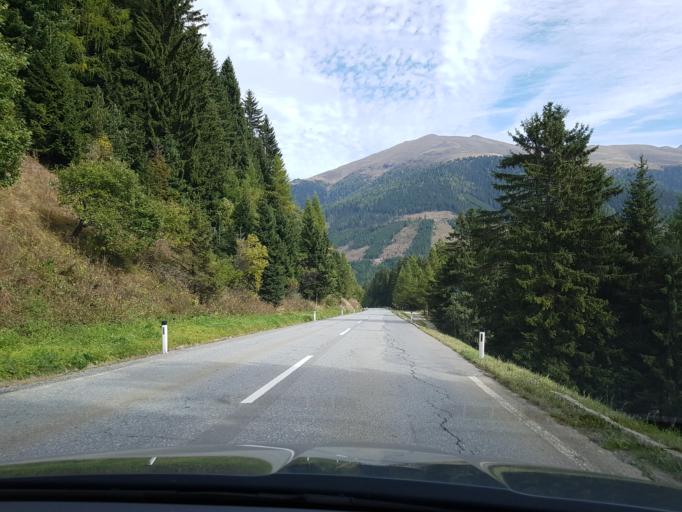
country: AT
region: Salzburg
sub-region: Politischer Bezirk Tamsweg
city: Ramingstein
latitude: 46.9360
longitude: 13.8773
